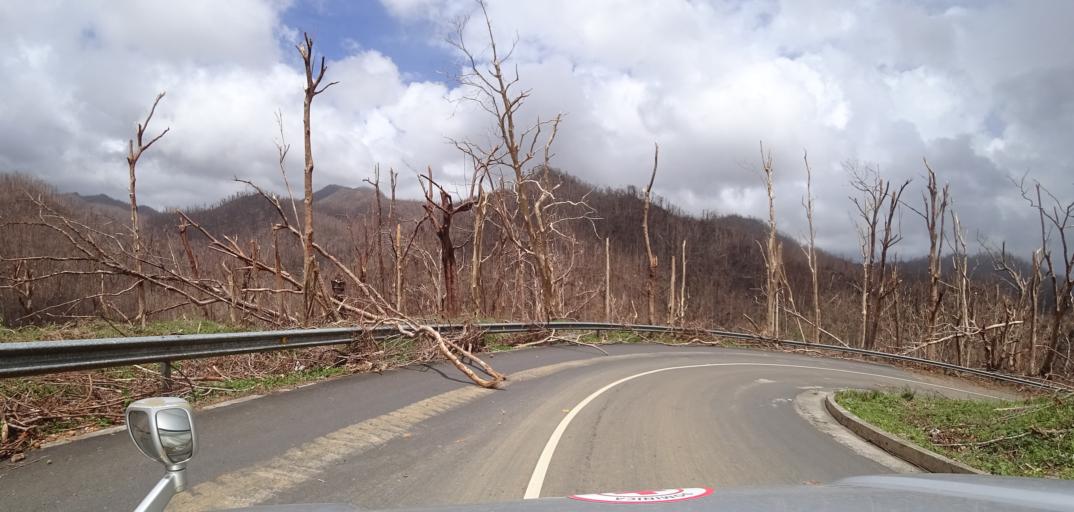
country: DM
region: Saint David
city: Castle Bruce
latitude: 15.4679
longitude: -61.3068
